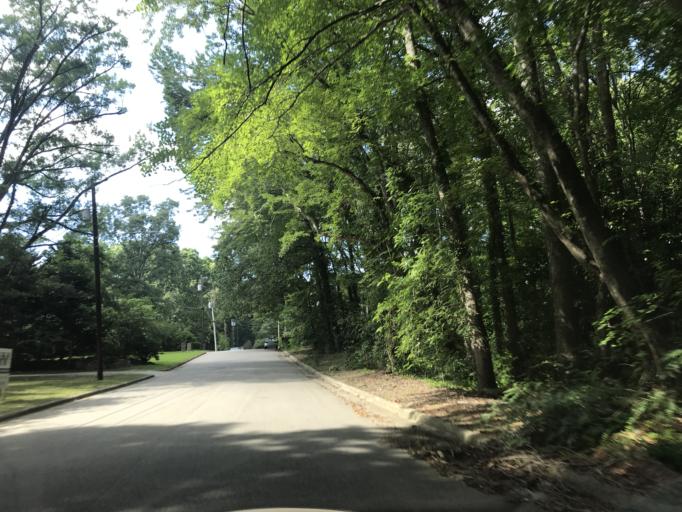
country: US
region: North Carolina
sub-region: Wake County
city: West Raleigh
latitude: 35.7842
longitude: -78.7155
